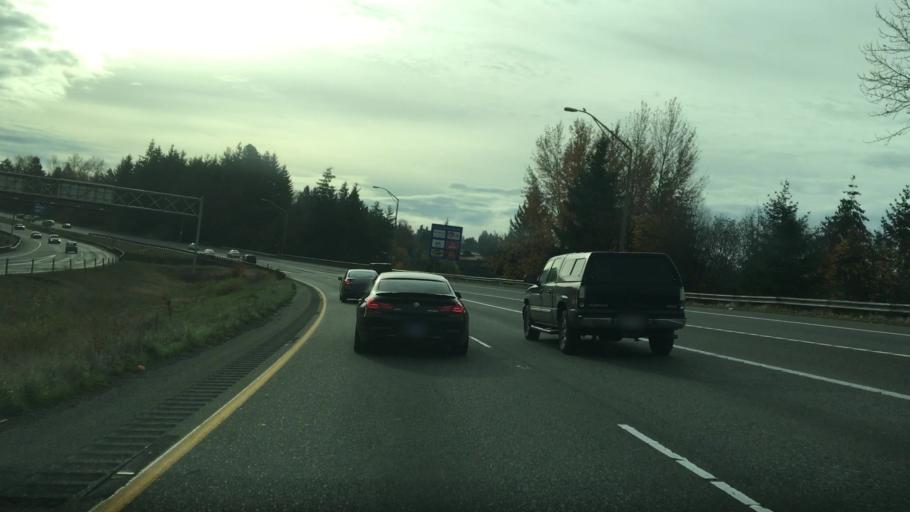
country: US
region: Washington
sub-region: Pierce County
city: Puyallup
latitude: 47.1786
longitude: -122.2960
